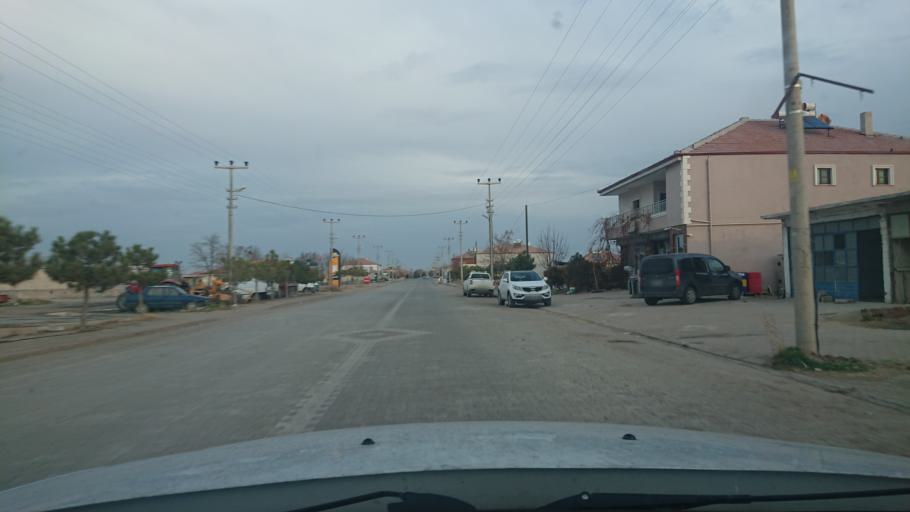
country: TR
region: Aksaray
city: Yesilova
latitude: 38.3372
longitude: 33.7510
